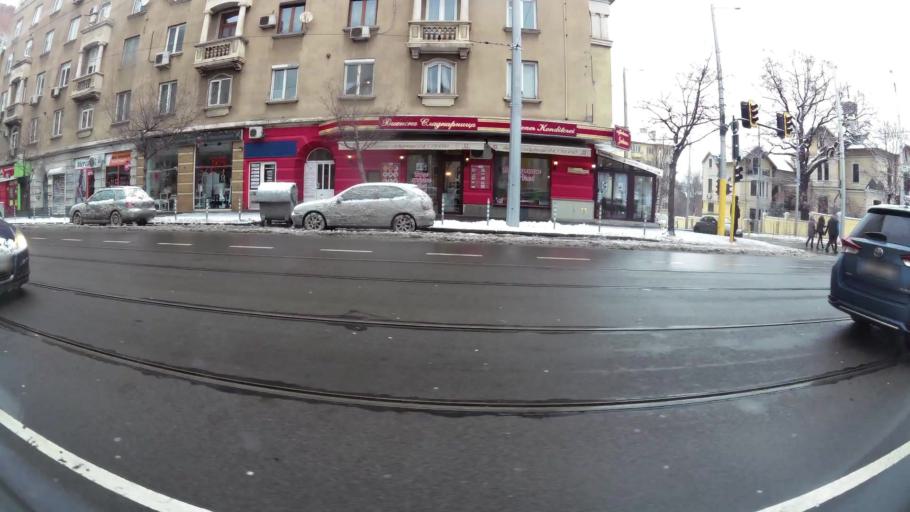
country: BG
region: Sofia-Capital
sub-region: Stolichna Obshtina
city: Sofia
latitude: 42.6987
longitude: 23.3344
